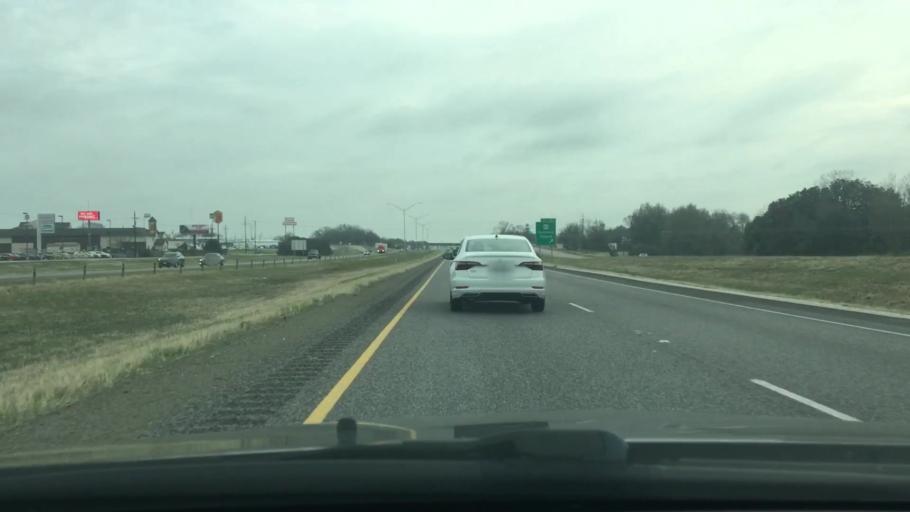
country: US
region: Texas
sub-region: Freestone County
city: Fairfield
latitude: 31.7221
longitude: -96.1790
